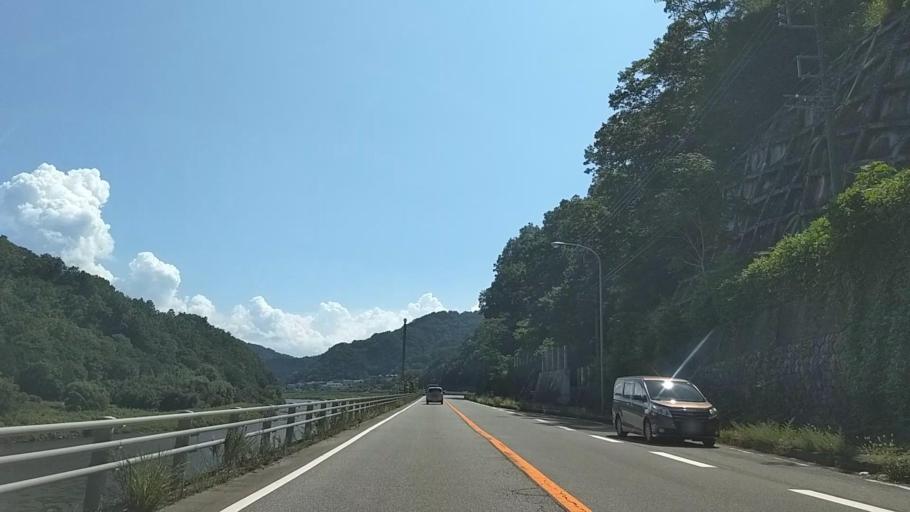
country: JP
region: Yamanashi
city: Ryuo
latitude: 35.5325
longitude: 138.4507
